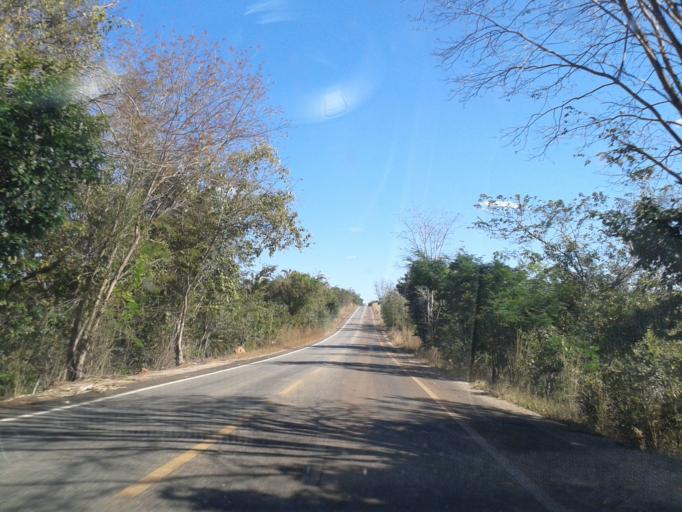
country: BR
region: Goias
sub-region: Mozarlandia
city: Mozarlandia
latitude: -14.4737
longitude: -50.4725
